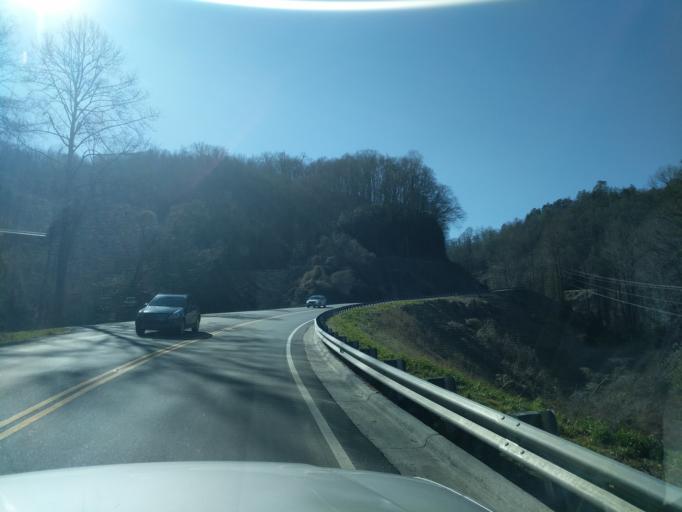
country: US
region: North Carolina
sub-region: Graham County
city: Robbinsville
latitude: 35.2533
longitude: -83.6971
